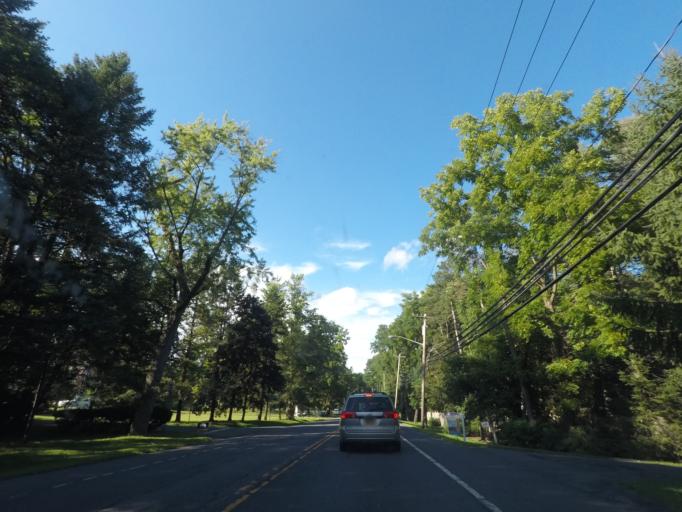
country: US
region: New York
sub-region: Albany County
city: West Albany
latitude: 42.6916
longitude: -73.7529
